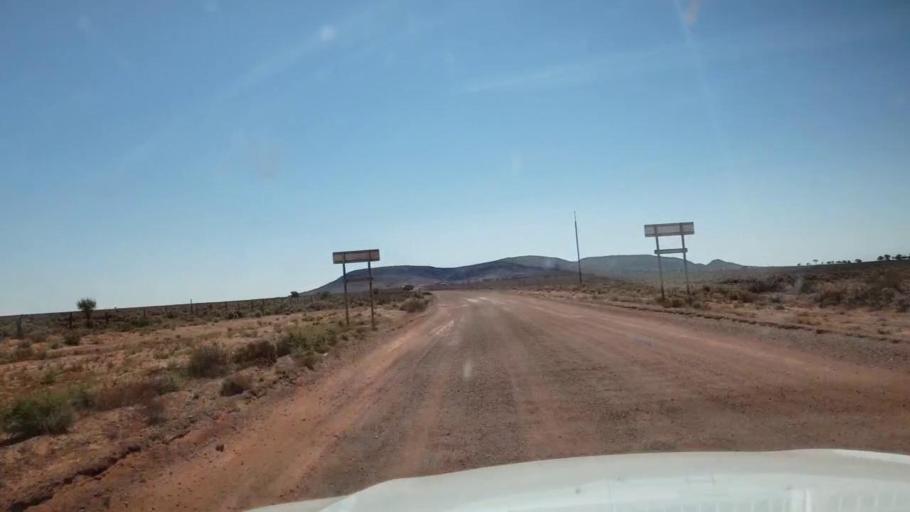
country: AU
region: South Australia
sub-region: Whyalla
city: Whyalla
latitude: -32.7131
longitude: 137.1417
